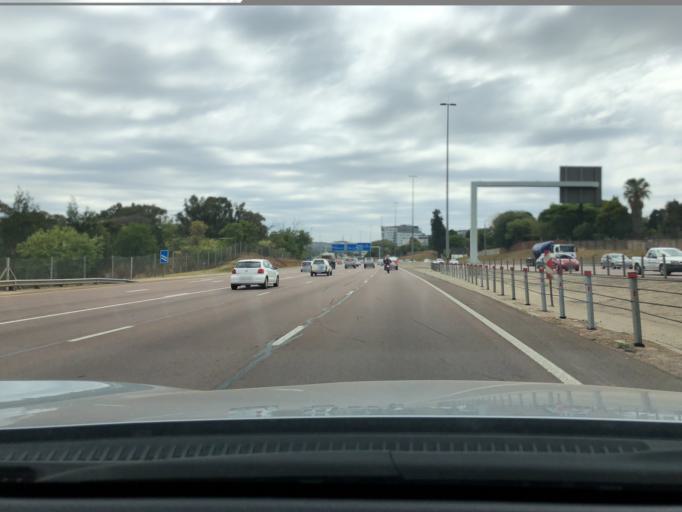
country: ZA
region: Gauteng
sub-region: City of Tshwane Metropolitan Municipality
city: Pretoria
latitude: -25.7927
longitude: 28.2675
